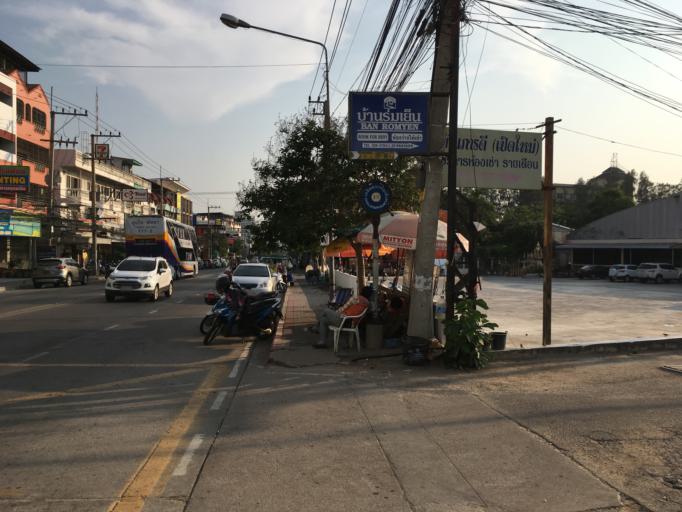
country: TH
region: Chon Buri
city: Phatthaya
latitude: 12.9474
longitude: 100.8965
